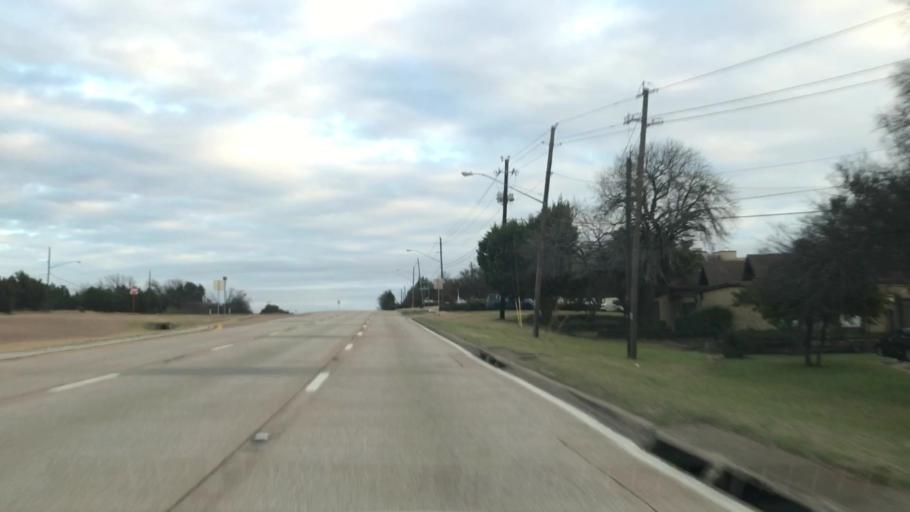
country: US
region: Texas
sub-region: Dallas County
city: Cockrell Hill
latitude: 32.6991
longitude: -96.8982
